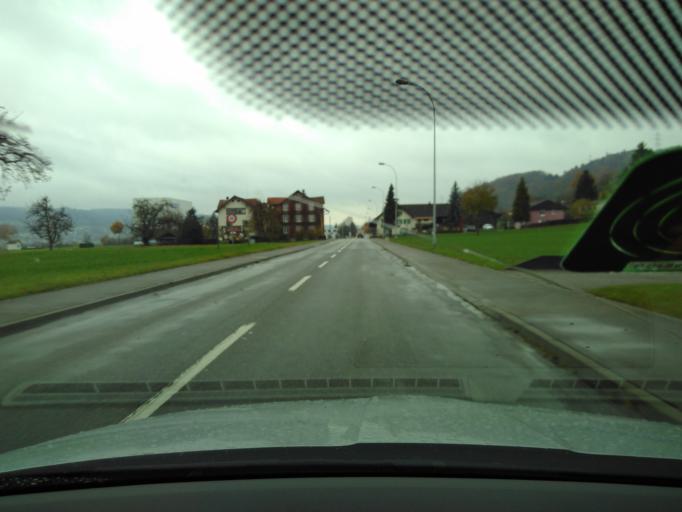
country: CH
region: Lucerne
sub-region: Sursee District
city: Triengen
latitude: 47.2414
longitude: 8.0726
